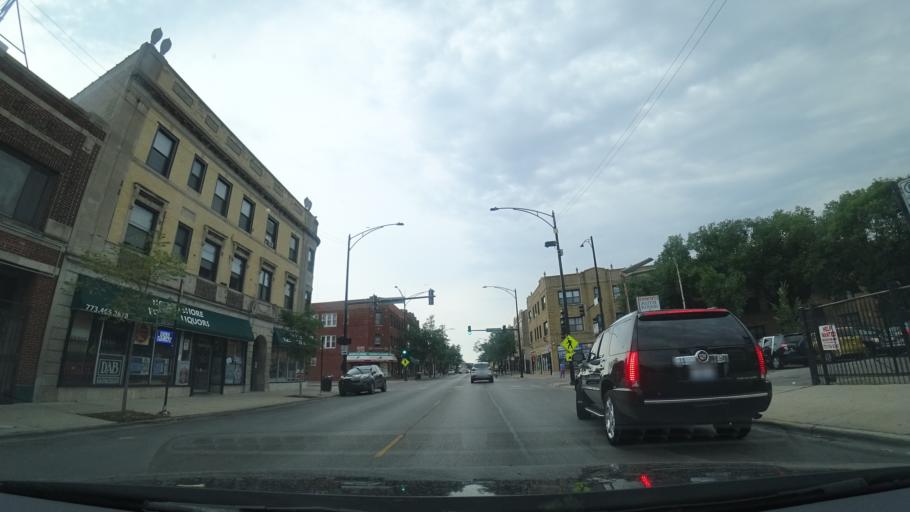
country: US
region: Illinois
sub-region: Cook County
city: Evanston
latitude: 42.0038
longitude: -87.6726
